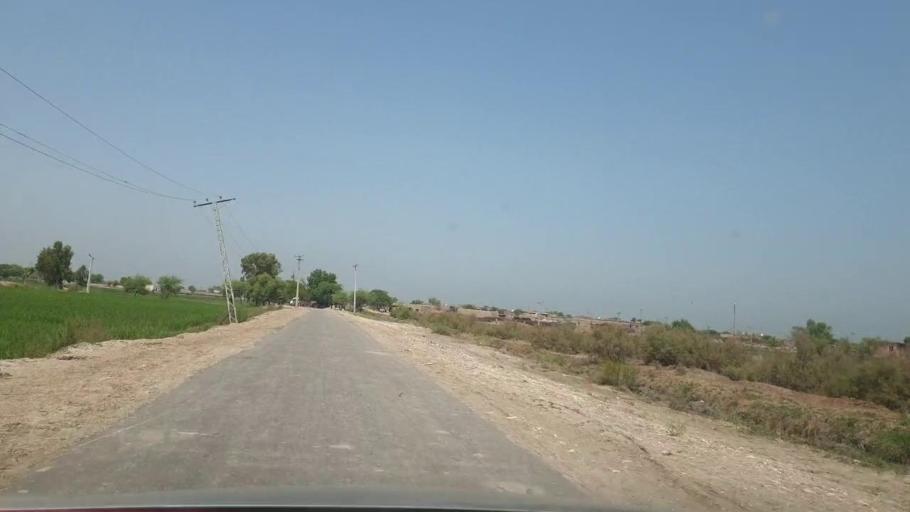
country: PK
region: Sindh
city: Warah
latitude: 27.4782
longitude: 67.7569
